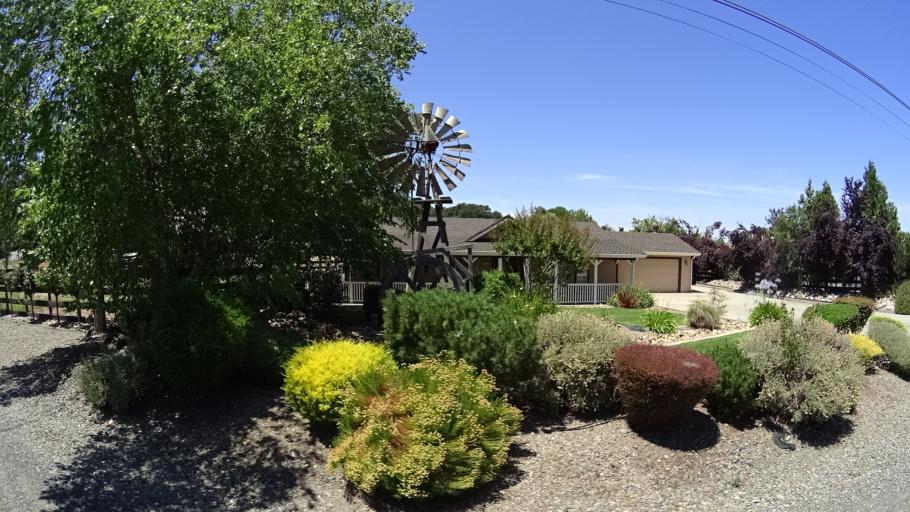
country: US
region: California
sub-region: Calaveras County
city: Rancho Calaveras
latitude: 38.1238
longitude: -120.8661
